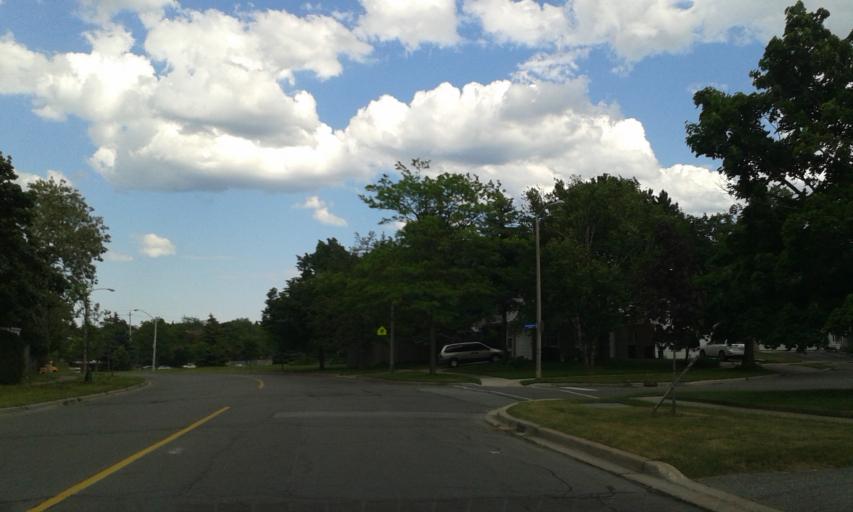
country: CA
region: Ontario
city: Scarborough
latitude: 43.8053
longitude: -79.2680
